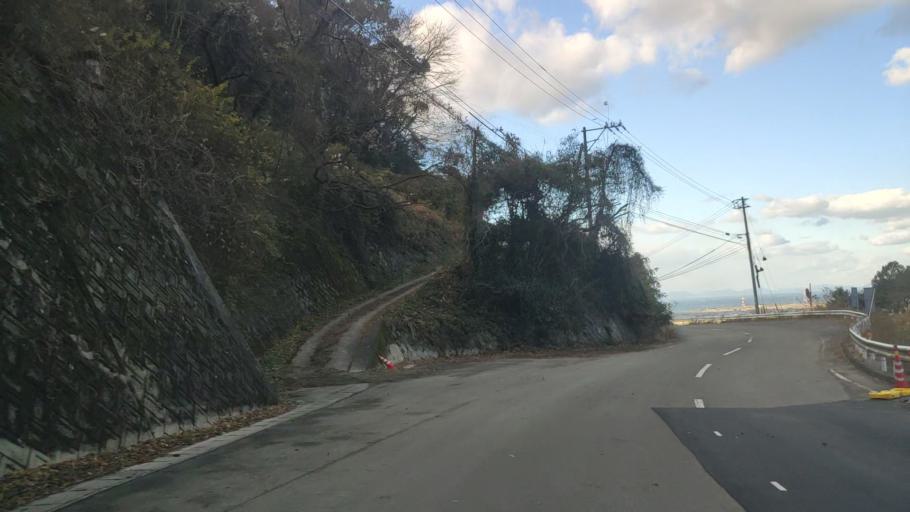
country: JP
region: Ehime
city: Saijo
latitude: 33.8790
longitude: 133.1335
